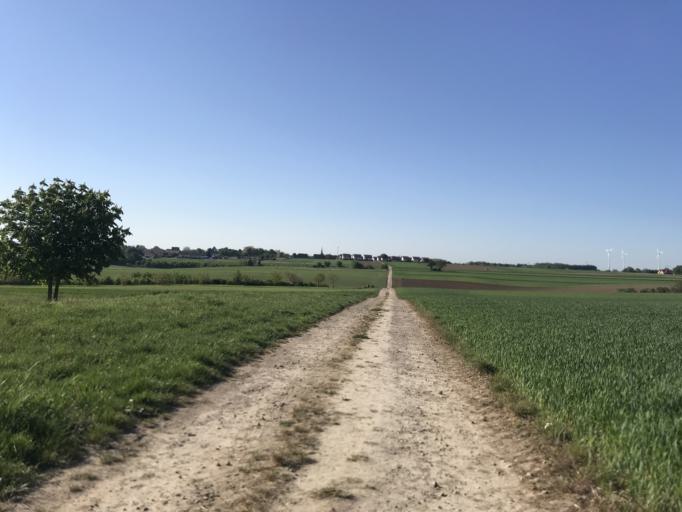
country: DE
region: Rheinland-Pfalz
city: Harxheim
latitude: 49.9244
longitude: 8.2406
